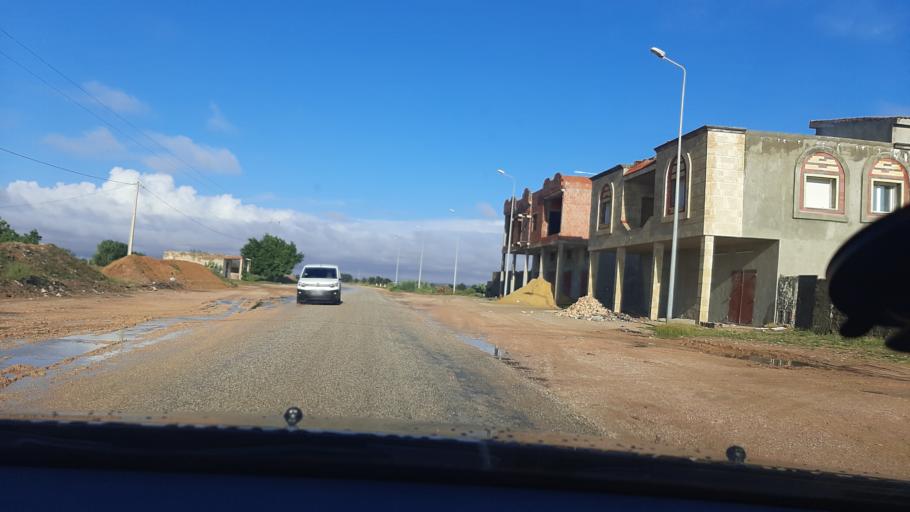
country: TN
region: Safaqis
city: Sfax
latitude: 34.8858
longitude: 10.6268
